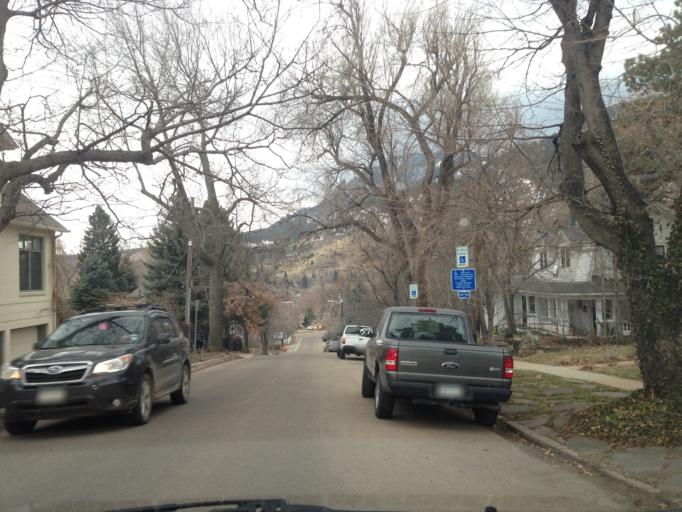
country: US
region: Colorado
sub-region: Boulder County
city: Boulder
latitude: 40.0184
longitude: -105.2915
